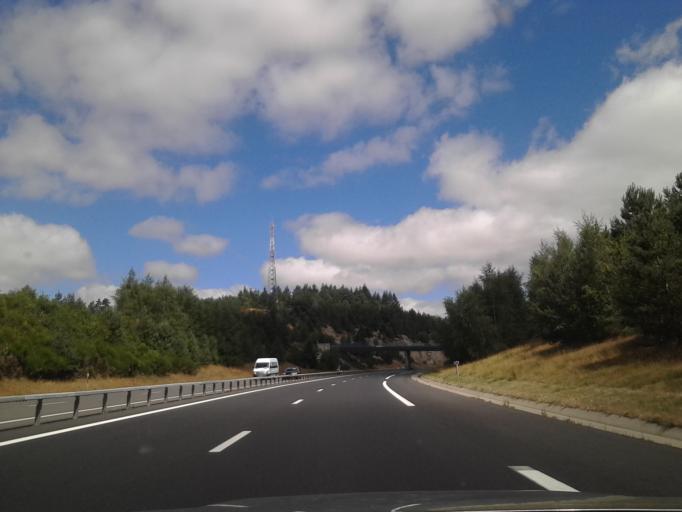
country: FR
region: Languedoc-Roussillon
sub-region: Departement de la Lozere
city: Marvejols
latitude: 44.6329
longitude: 3.2415
